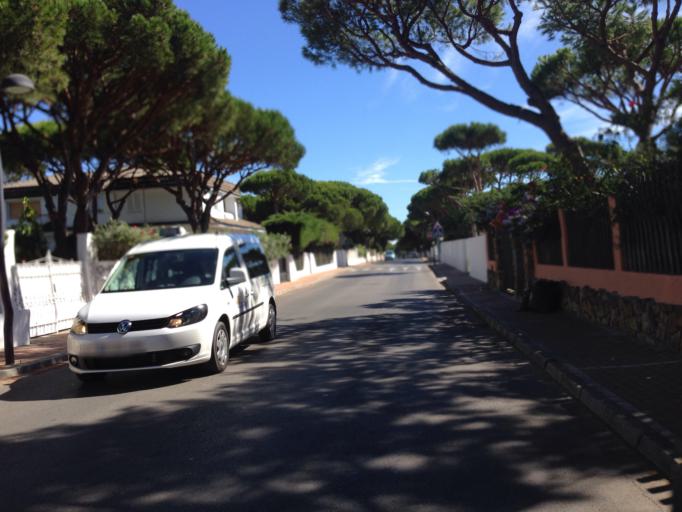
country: ES
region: Andalusia
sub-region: Provincia de Cadiz
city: Conil de la Frontera
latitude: 36.3193
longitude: -6.1525
